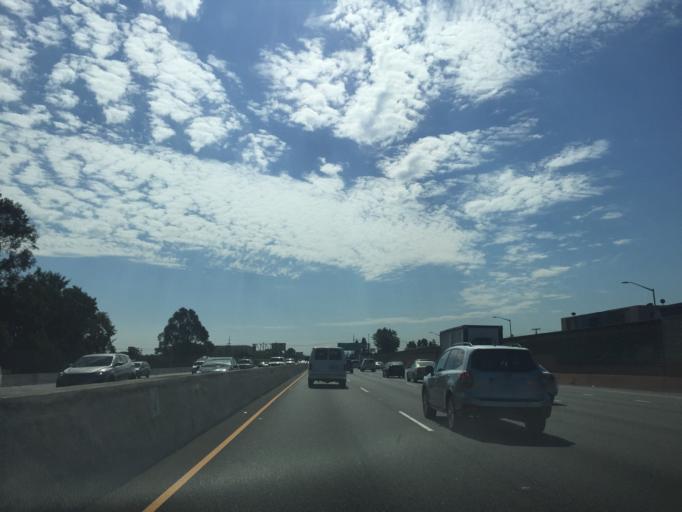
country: US
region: California
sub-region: San Mateo County
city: San Mateo
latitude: 37.5831
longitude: -122.3274
